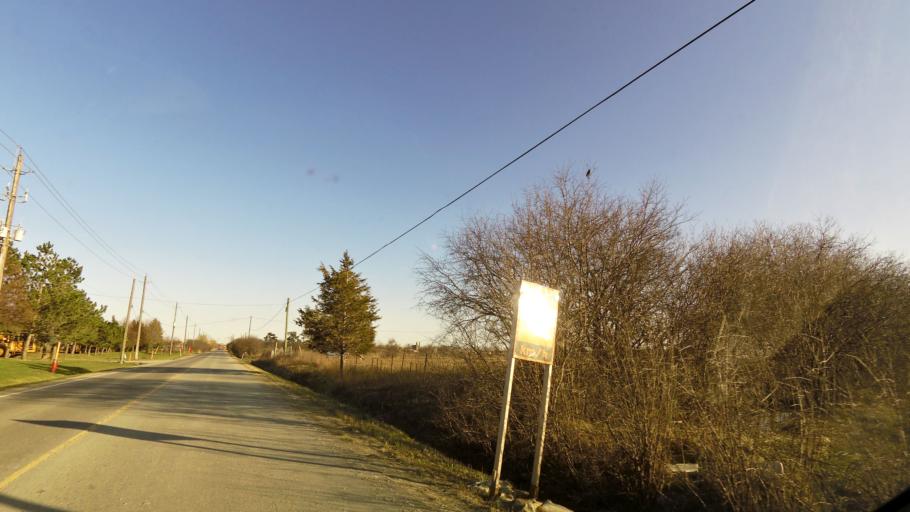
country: CA
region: Ontario
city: Brampton
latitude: 43.8229
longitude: -79.6843
